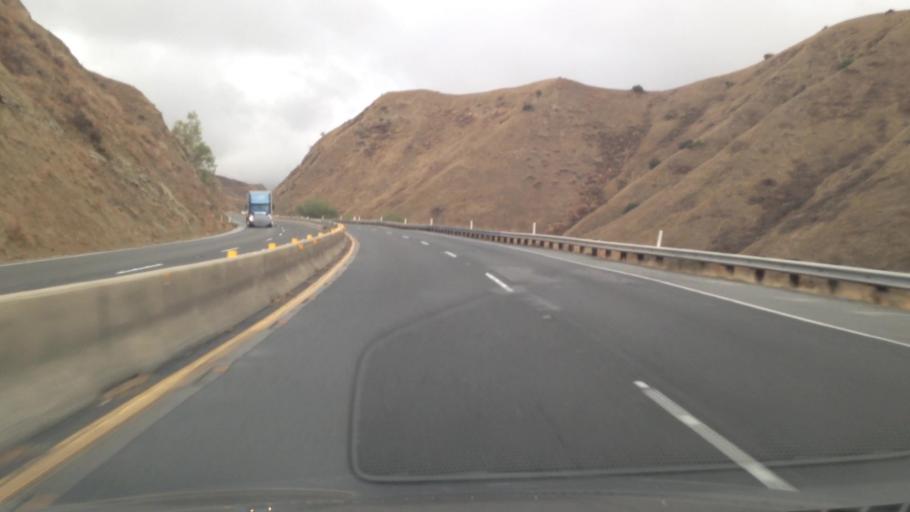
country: US
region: California
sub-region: Riverside County
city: Calimesa
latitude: 33.9400
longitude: -117.0930
